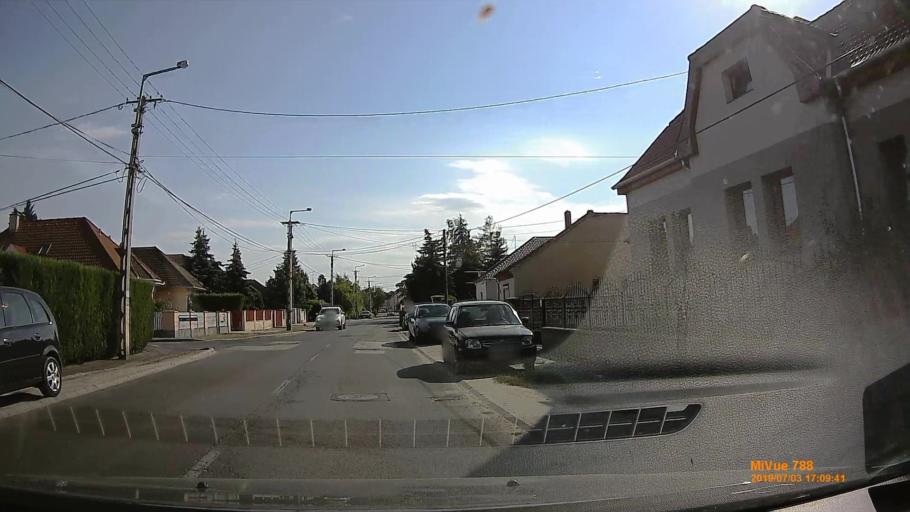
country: HU
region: Gyor-Moson-Sopron
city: Gyor
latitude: 47.7073
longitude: 17.6463
